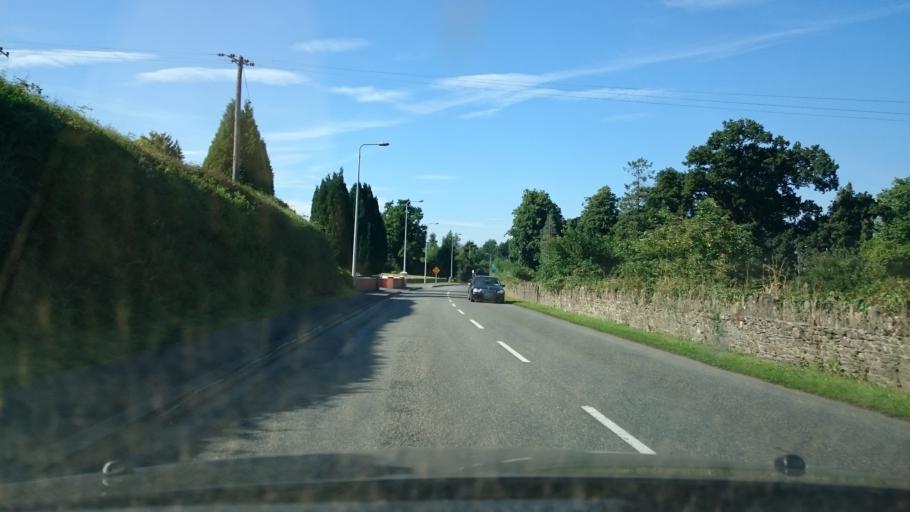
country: IE
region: Leinster
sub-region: Kilkenny
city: Graiguenamanagh
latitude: 52.5354
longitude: -6.9623
